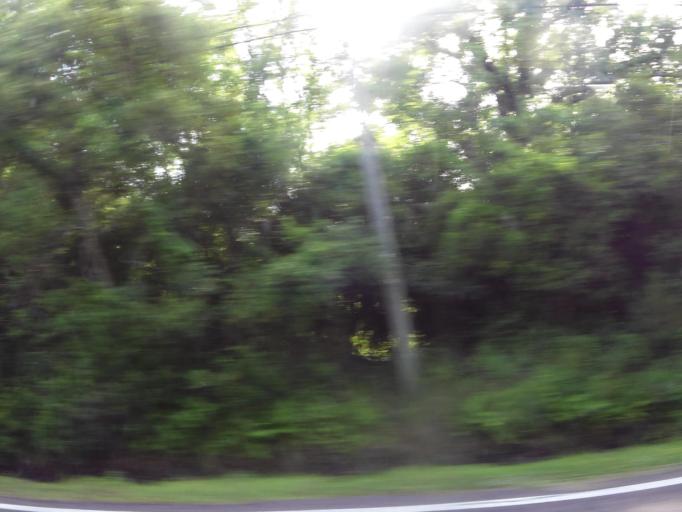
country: US
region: Florida
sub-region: Nassau County
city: Fernandina Beach
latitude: 30.5296
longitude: -81.4845
